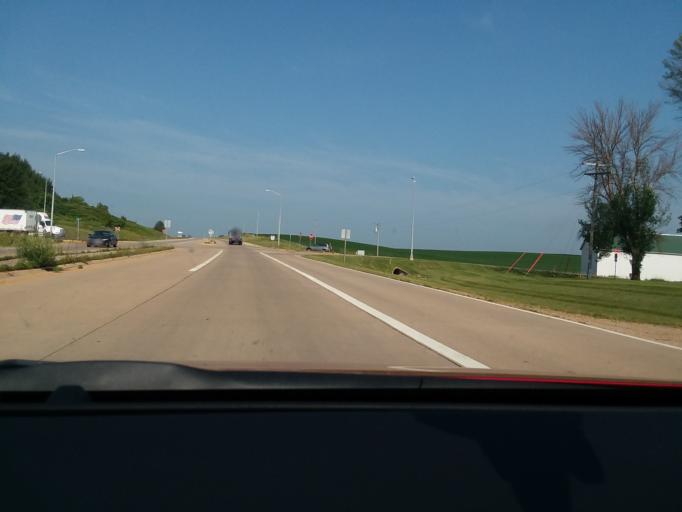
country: US
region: Wisconsin
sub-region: Dane County
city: Windsor
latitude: 43.1951
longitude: -89.3644
